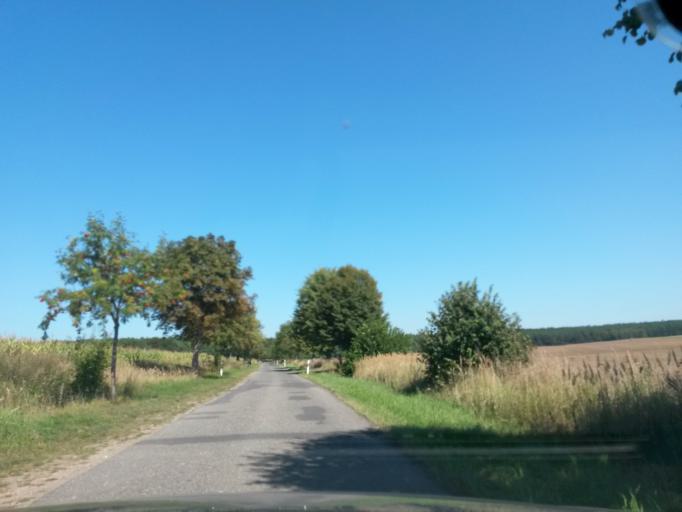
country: DE
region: Brandenburg
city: Templin
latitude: 53.1808
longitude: 13.4400
